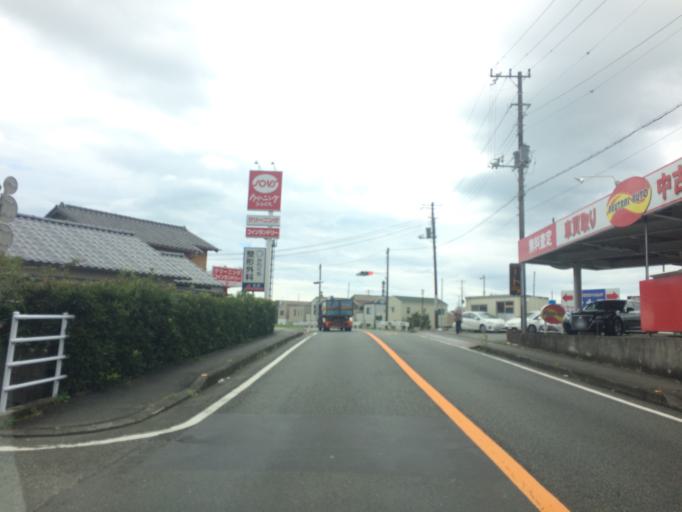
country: JP
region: Shizuoka
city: Fuji
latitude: 35.1451
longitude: 138.6468
